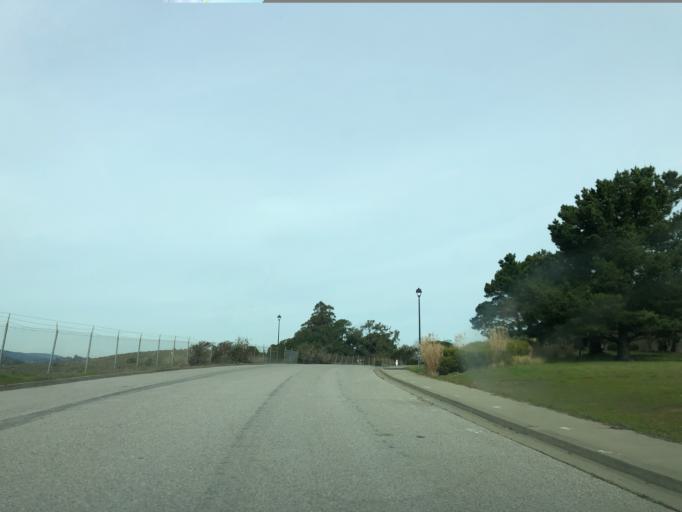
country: US
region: California
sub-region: San Mateo County
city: Highlands-Baywood Park
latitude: 37.5047
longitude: -122.3207
